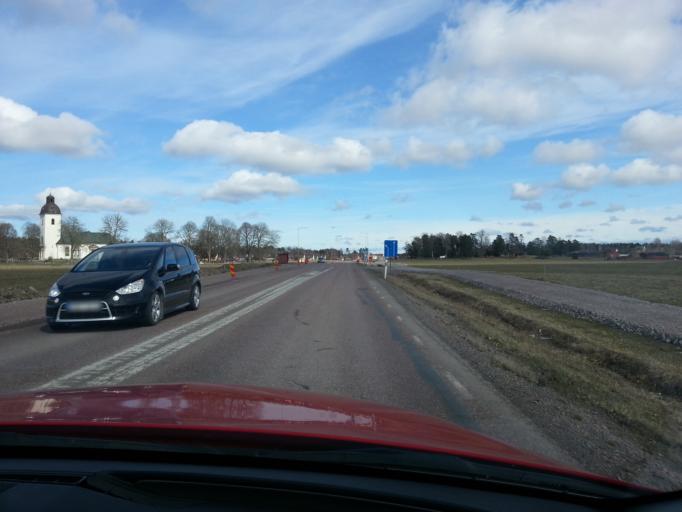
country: SE
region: Uppsala
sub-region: Osthammars Kommun
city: Gimo
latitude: 60.0573
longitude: 18.0656
